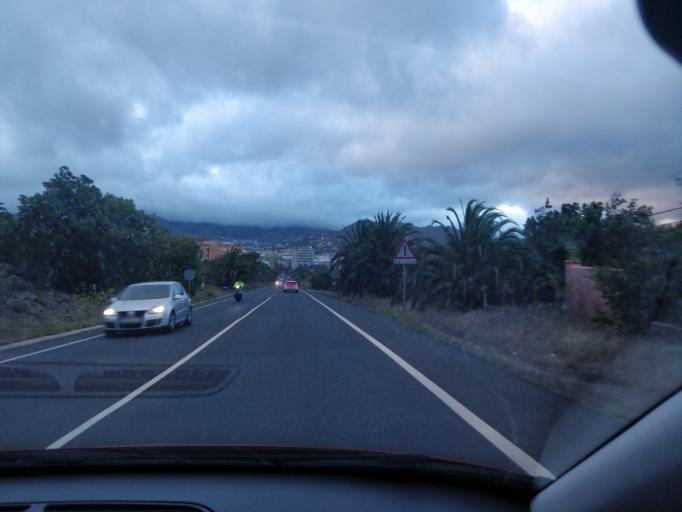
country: ES
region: Canary Islands
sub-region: Provincia de Santa Cruz de Tenerife
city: La Laguna
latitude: 28.4763
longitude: -16.3217
